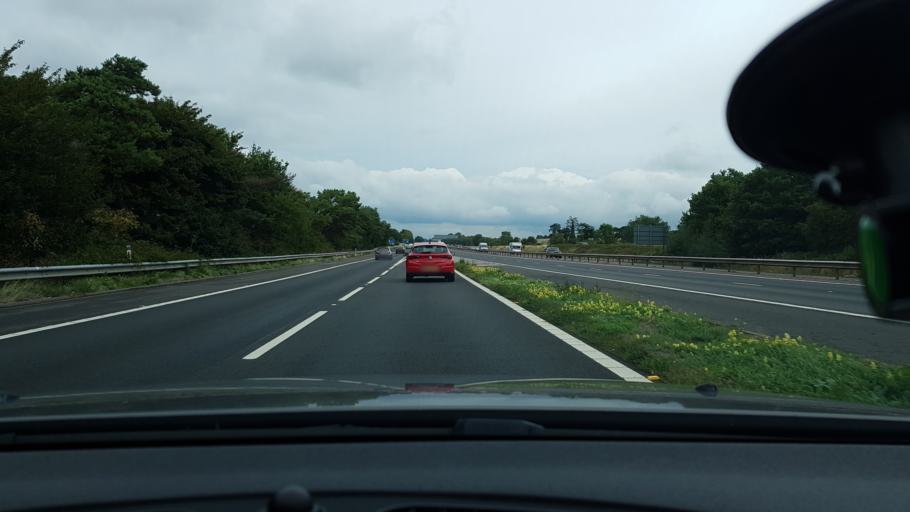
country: GB
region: England
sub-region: Hampshire
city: Overton
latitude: 51.2070
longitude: -1.1820
